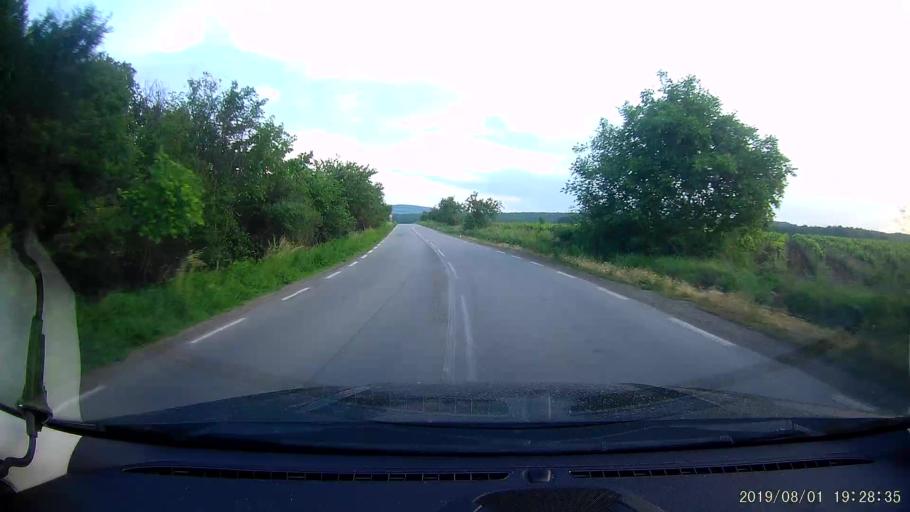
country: BG
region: Burgas
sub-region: Obshtina Sungurlare
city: Sungurlare
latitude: 42.8406
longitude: 26.9148
